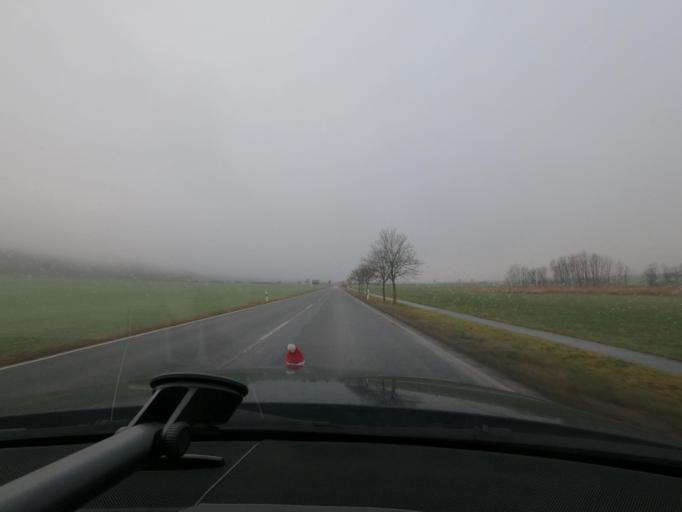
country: DE
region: Thuringia
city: Wingerode
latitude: 51.3792
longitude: 10.2517
